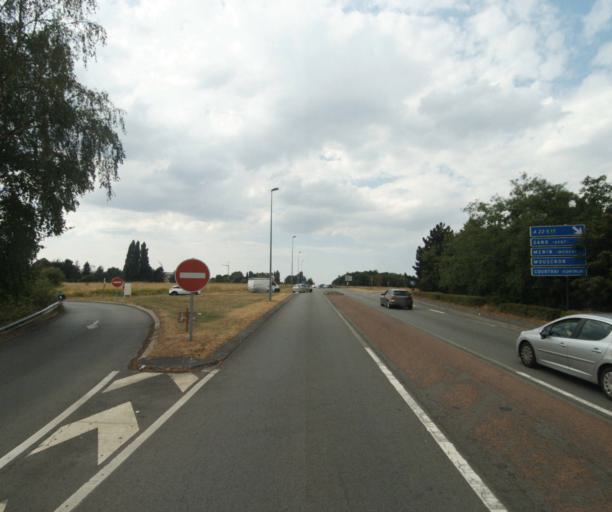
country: FR
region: Nord-Pas-de-Calais
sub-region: Departement du Nord
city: Neuville-en-Ferrain
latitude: 50.7605
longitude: 3.1598
